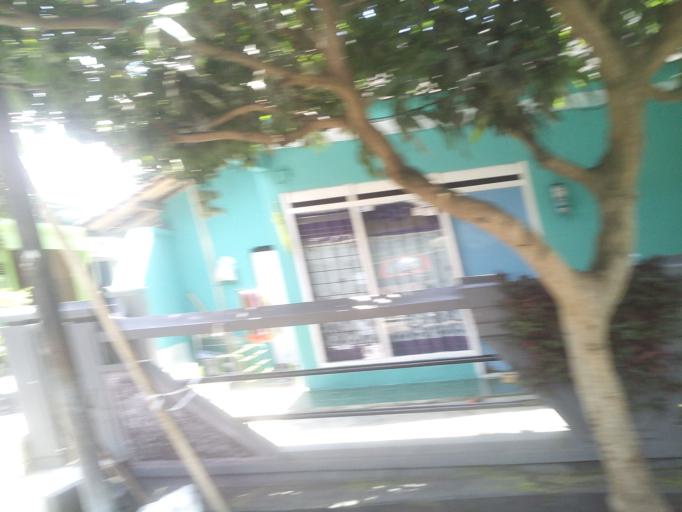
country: ID
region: East Java
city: Kloncing
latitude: -8.1901
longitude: 113.7225
